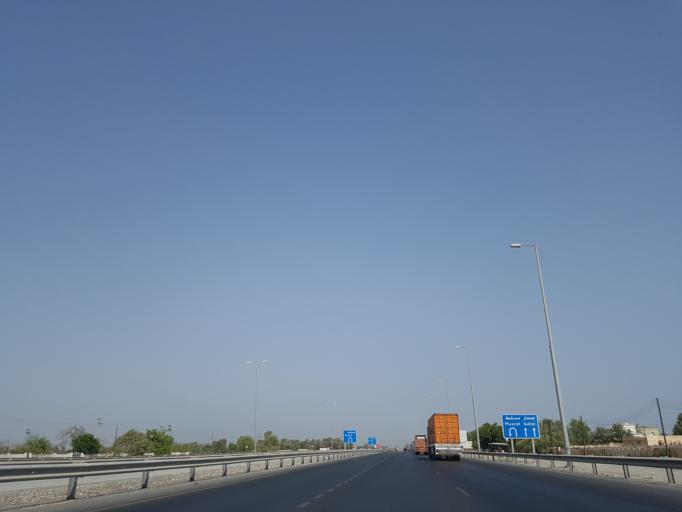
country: OM
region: Al Batinah
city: As Suwayq
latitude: 23.7607
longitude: 57.5558
